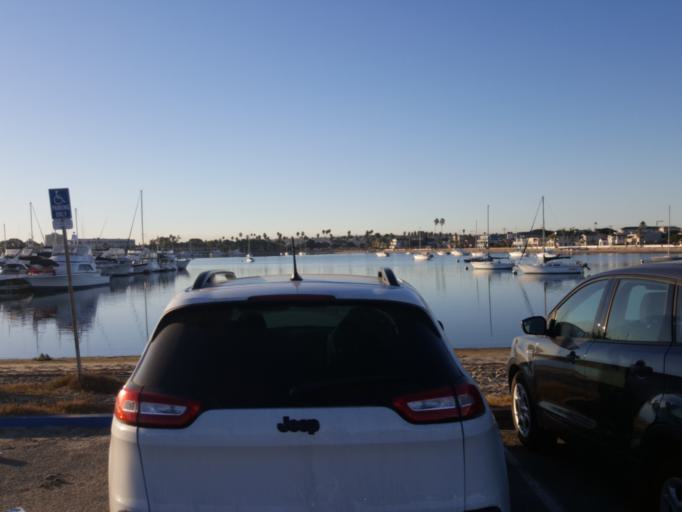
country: US
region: California
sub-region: San Diego County
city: La Jolla
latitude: 32.7785
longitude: -117.2505
